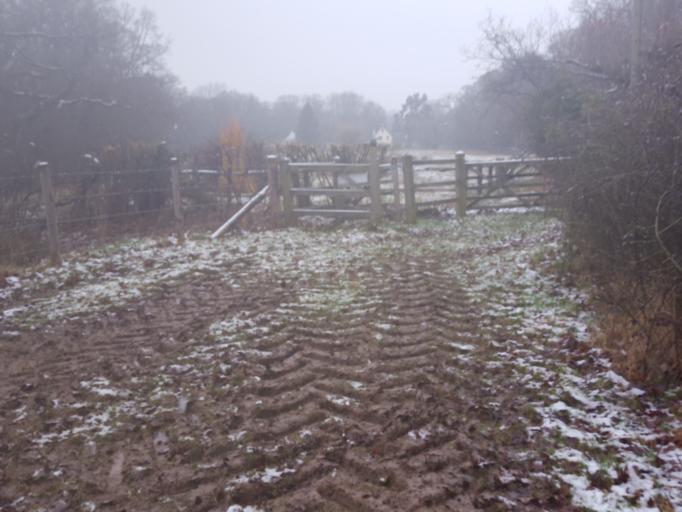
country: GB
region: England
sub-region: West Sussex
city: Gossops Green
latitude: 51.1276
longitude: -0.2291
